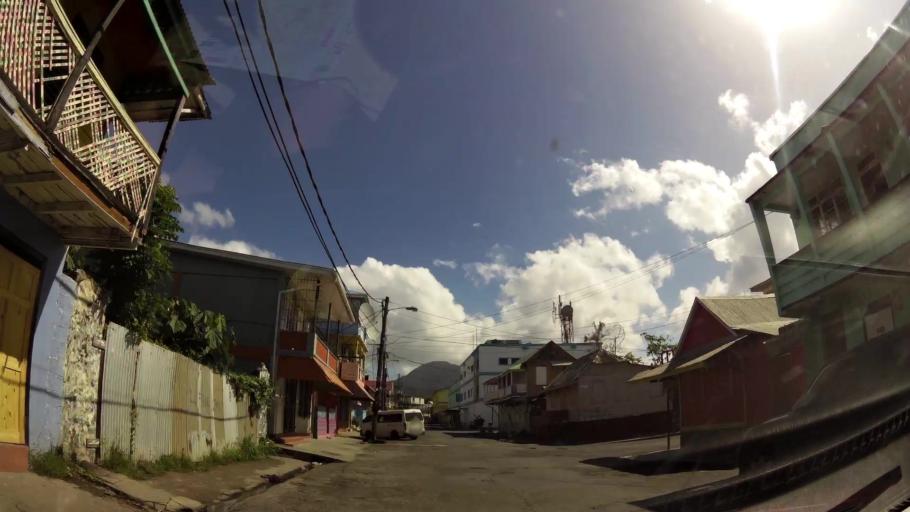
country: DM
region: Saint George
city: Roseau
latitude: 15.2993
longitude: -61.3892
